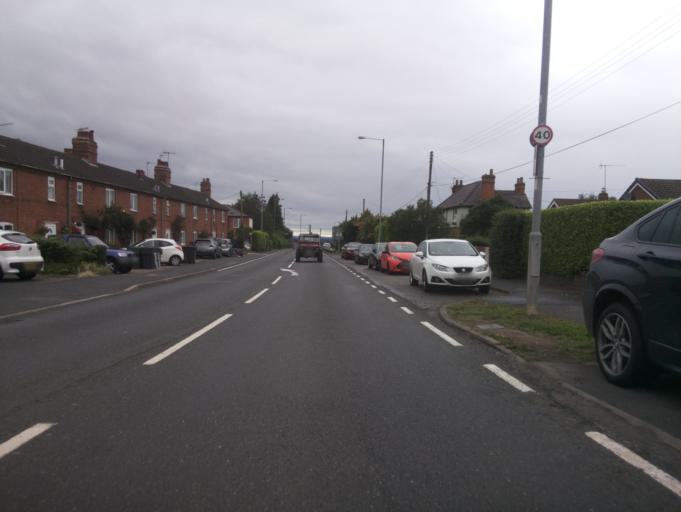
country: GB
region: England
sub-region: Worcestershire
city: Bromsgrove
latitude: 52.3142
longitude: -2.0793
